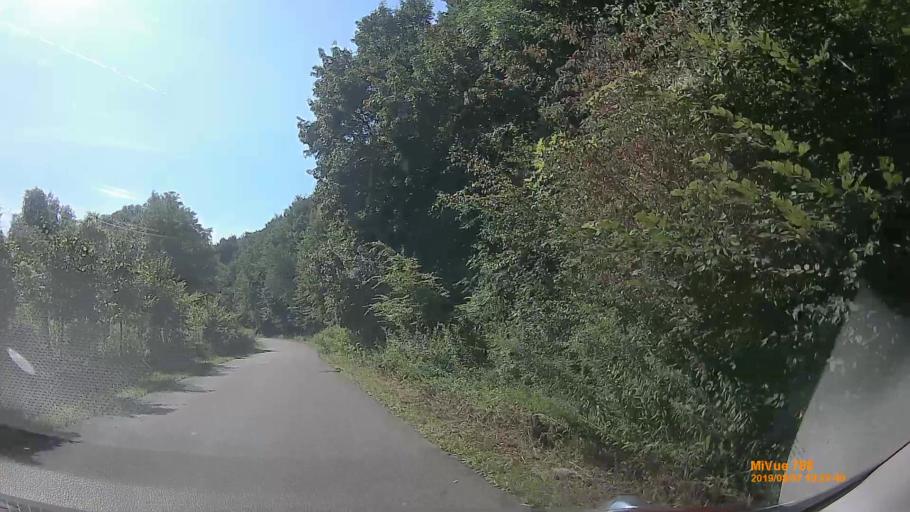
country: HU
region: Veszprem
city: Ajka
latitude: 47.0805
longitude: 17.5757
